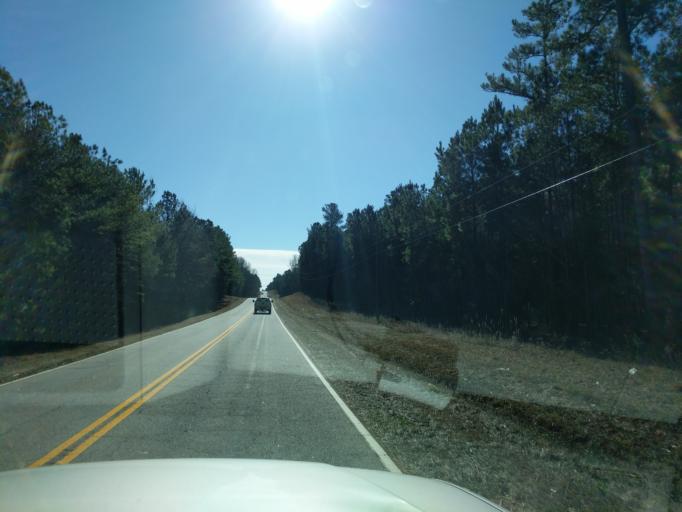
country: US
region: South Carolina
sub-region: Saluda County
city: Saluda
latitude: 34.1429
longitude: -81.8455
